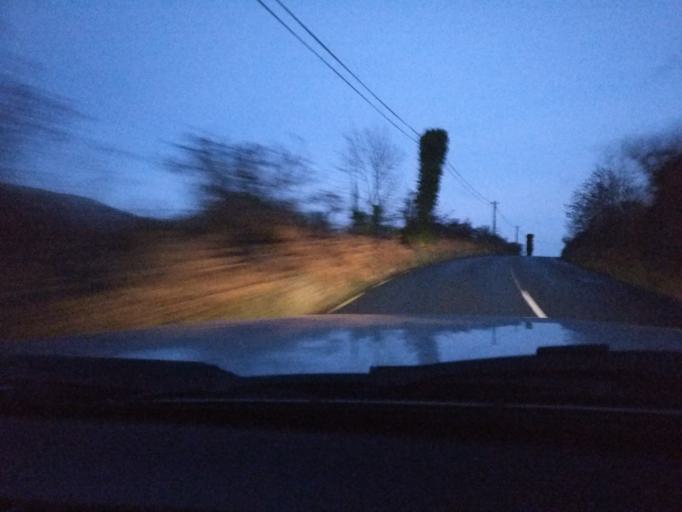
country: GB
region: Northern Ireland
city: Rostrevor
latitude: 54.0683
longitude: -6.2249
